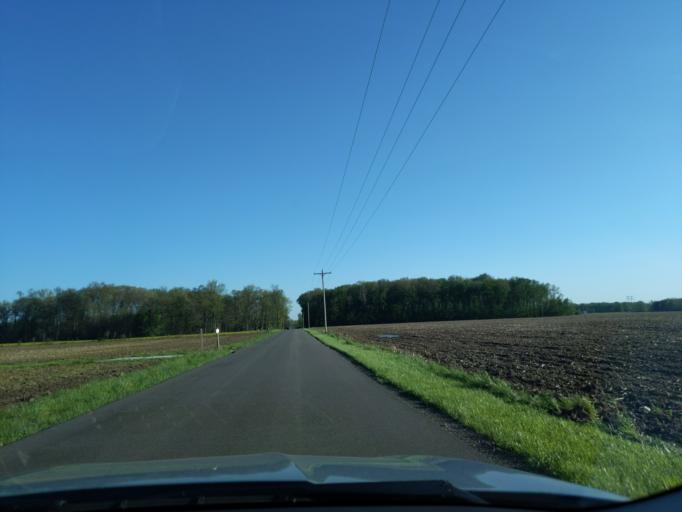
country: US
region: Indiana
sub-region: Decatur County
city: Westport
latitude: 39.1959
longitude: -85.5458
